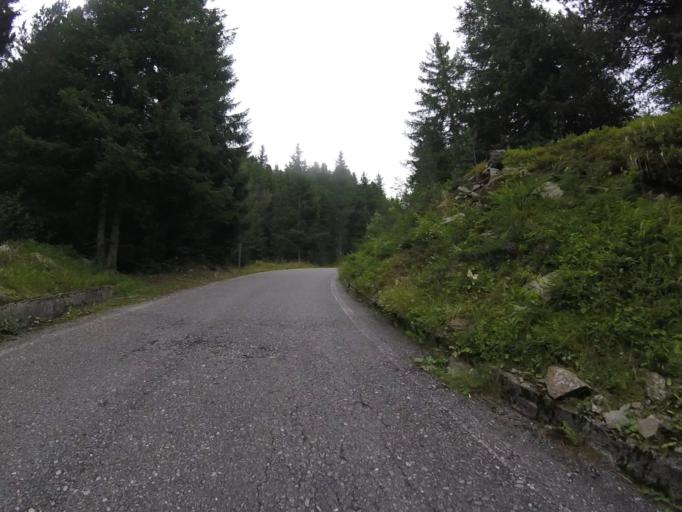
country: IT
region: Lombardy
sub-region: Provincia di Sondrio
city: Mazzo di Valtellina
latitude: 46.2481
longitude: 10.2890
